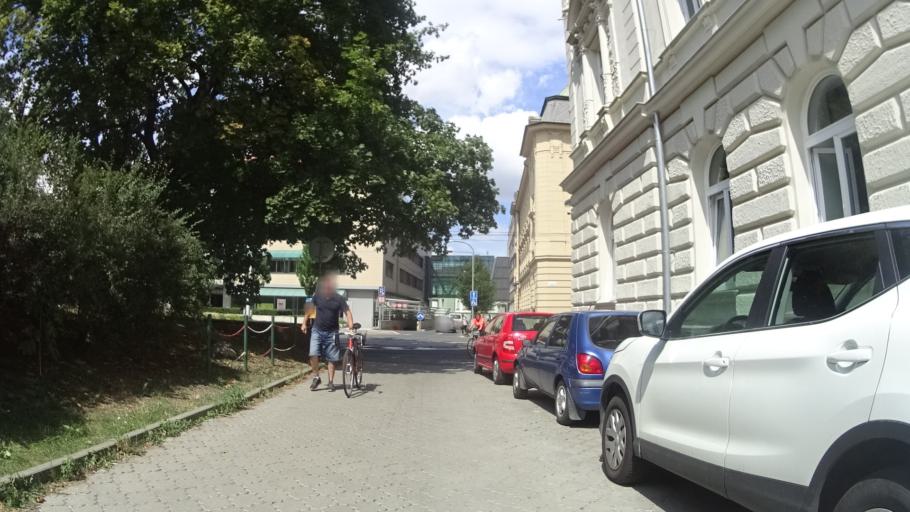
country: CZ
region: Olomoucky
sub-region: Okres Olomouc
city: Olomouc
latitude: 49.5955
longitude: 17.2444
